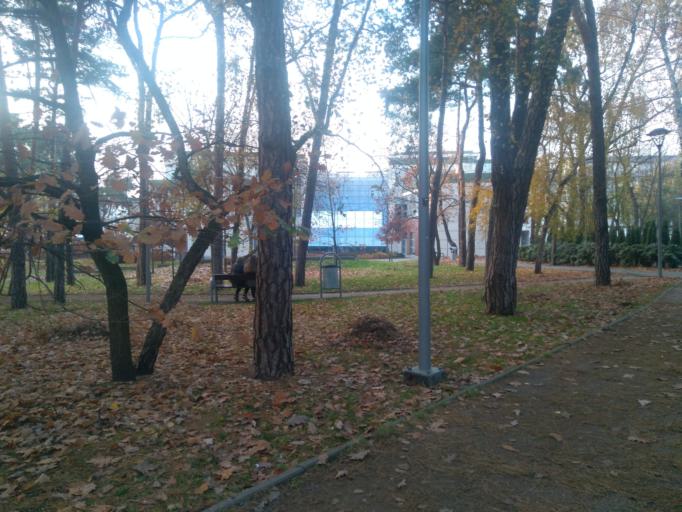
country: PL
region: Masovian Voivodeship
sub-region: Powiat legionowski
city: Legionowo
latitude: 52.3946
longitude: 20.9322
